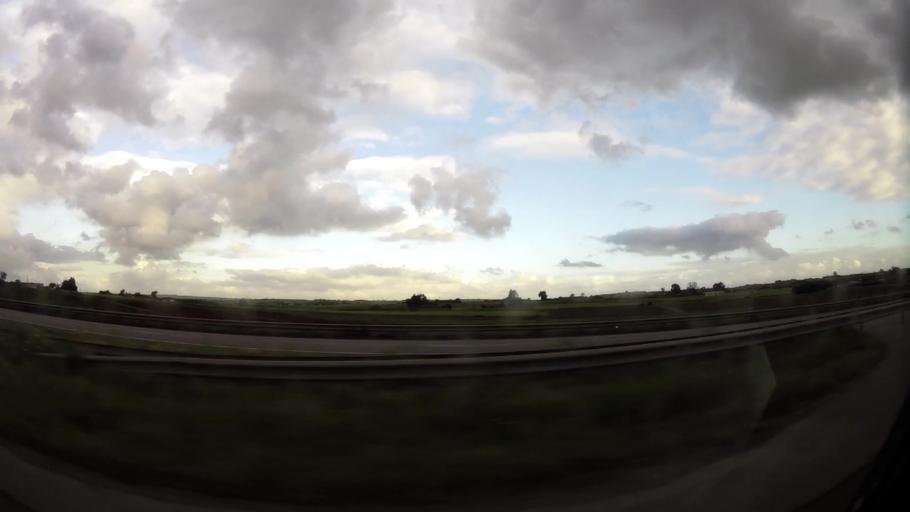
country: MA
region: Grand Casablanca
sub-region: Mediouna
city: Tit Mellil
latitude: 33.5908
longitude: -7.4495
